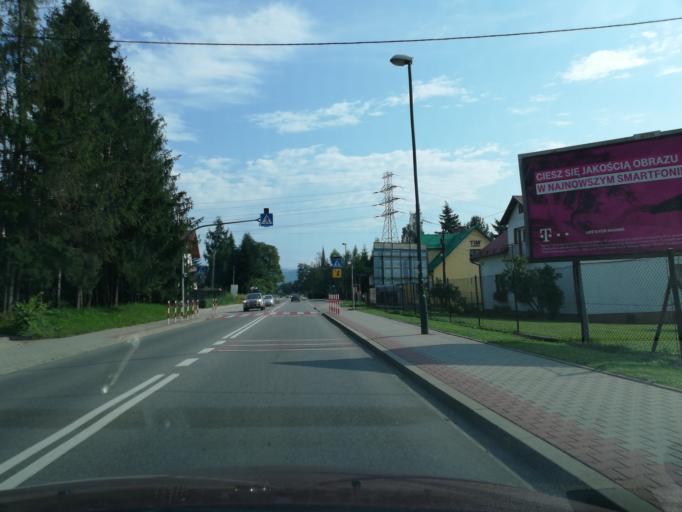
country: PL
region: Lesser Poland Voivodeship
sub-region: Powiat nowosadecki
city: Nawojowa
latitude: 49.5859
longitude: 20.7257
